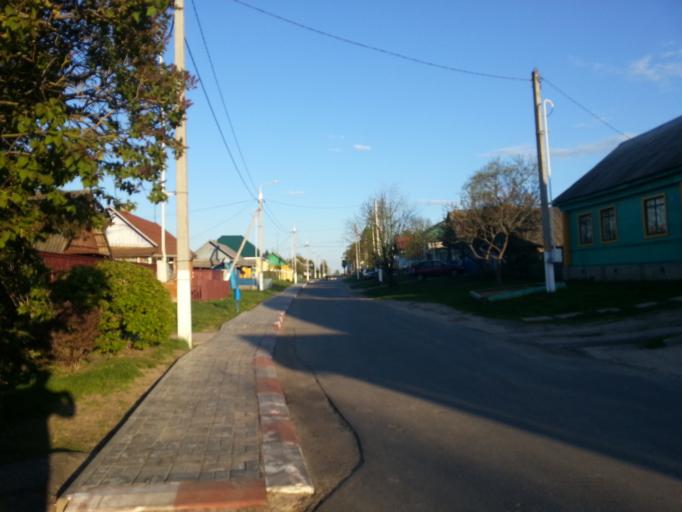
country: BY
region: Mogilev
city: Mstsislaw
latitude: 54.0239
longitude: 31.7289
